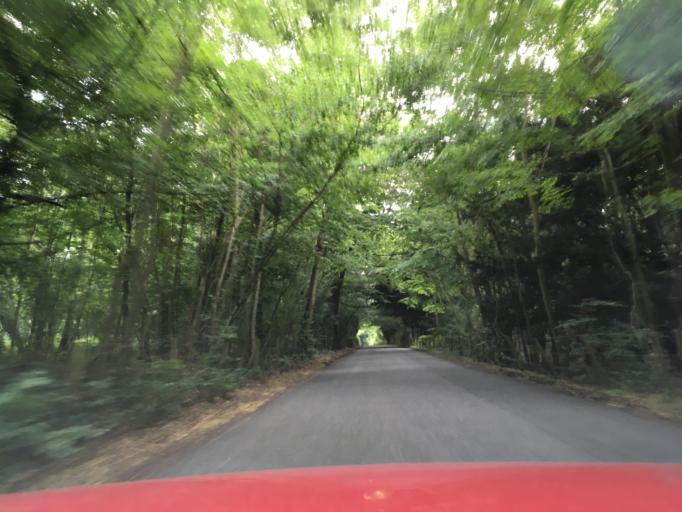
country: GB
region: England
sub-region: Hampshire
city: Bishops Waltham
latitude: 51.0211
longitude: -1.2357
